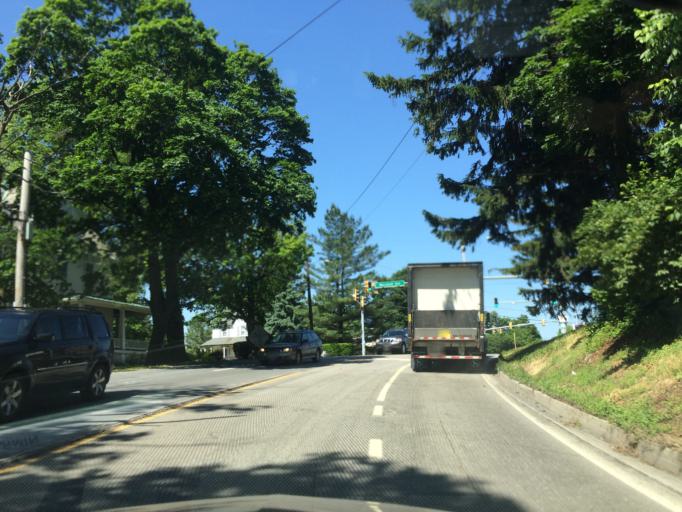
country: US
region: Maryland
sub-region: Frederick County
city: Braddock Heights
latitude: 39.4242
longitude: -77.5026
